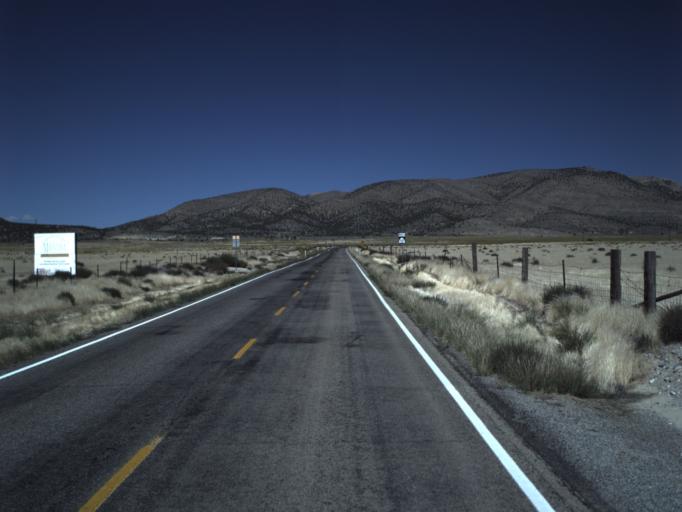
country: US
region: Utah
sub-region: Utah County
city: Eagle Mountain
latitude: 40.1575
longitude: -111.9496
